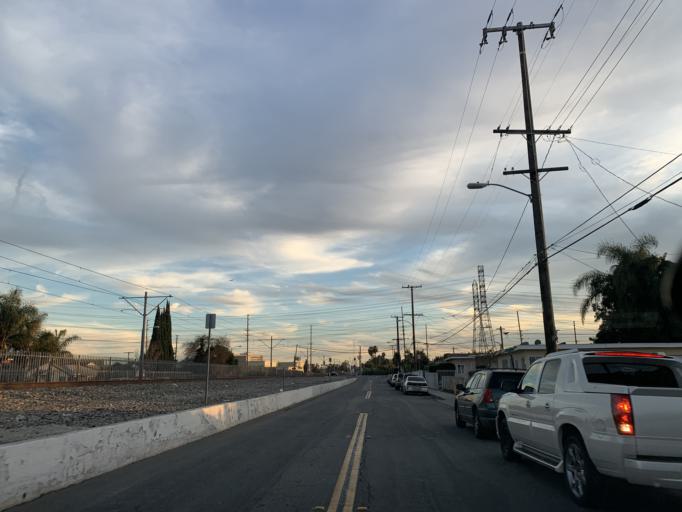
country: US
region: California
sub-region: Los Angeles County
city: Compton
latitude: 33.8829
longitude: -118.2235
